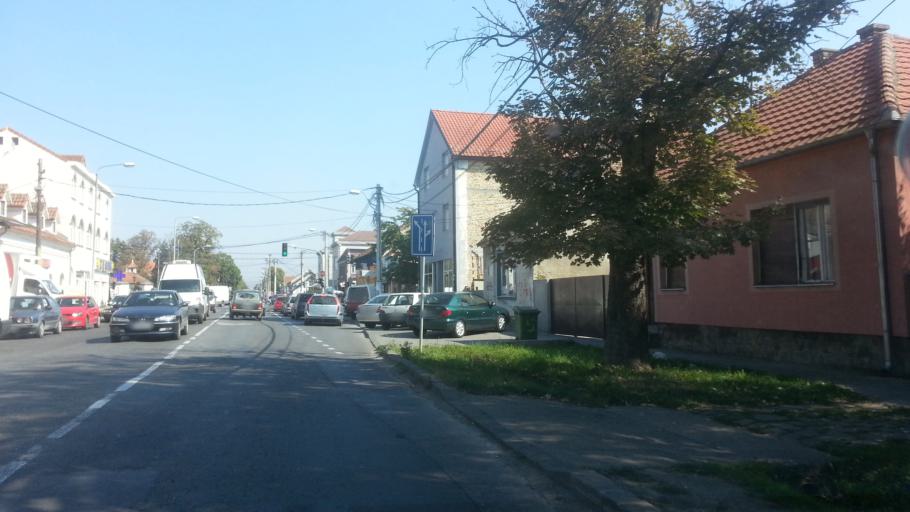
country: RS
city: Novi Banovci
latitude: 44.9055
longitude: 20.2741
